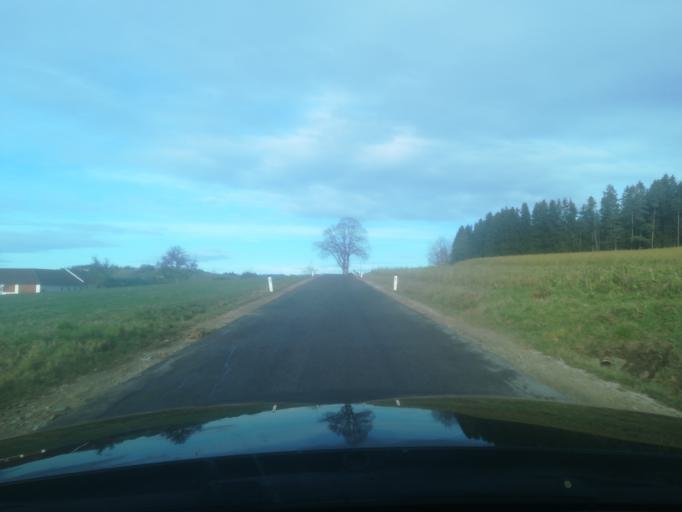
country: AT
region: Upper Austria
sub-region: Politischer Bezirk Perg
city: Perg
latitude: 48.3630
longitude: 14.6321
